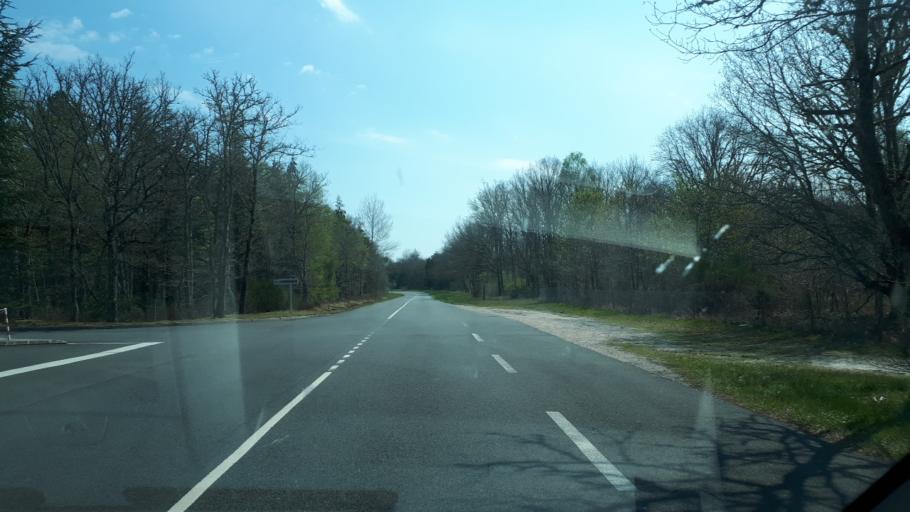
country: FR
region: Centre
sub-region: Departement du Loir-et-Cher
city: Selles-Saint-Denis
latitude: 47.3386
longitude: 1.9181
